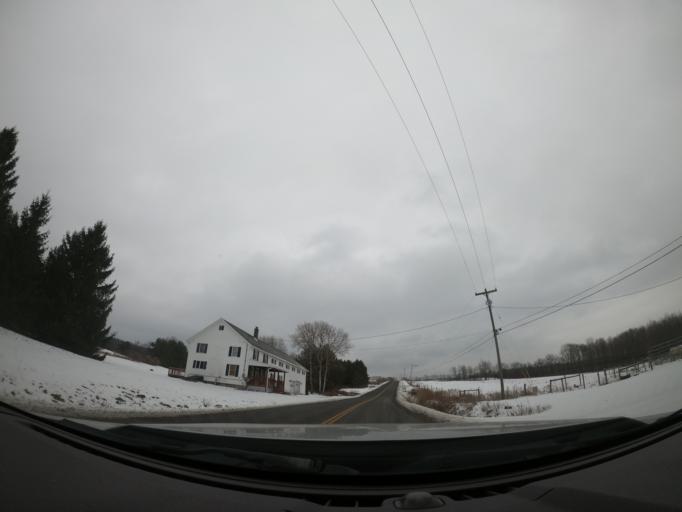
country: US
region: New York
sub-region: Cayuga County
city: Moravia
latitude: 42.7587
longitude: -76.3581
